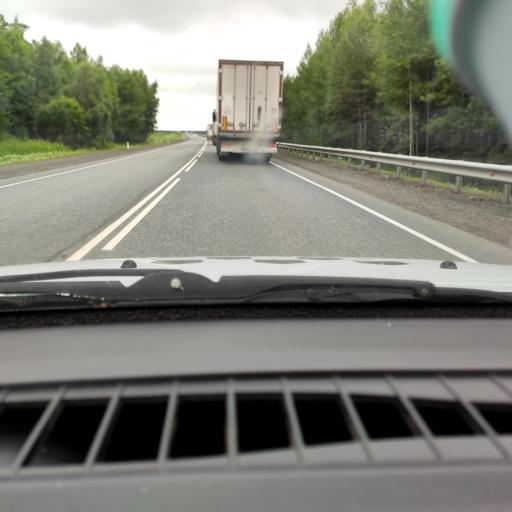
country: RU
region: Udmurtiya
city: Alnashi
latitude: 56.1079
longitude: 52.4602
